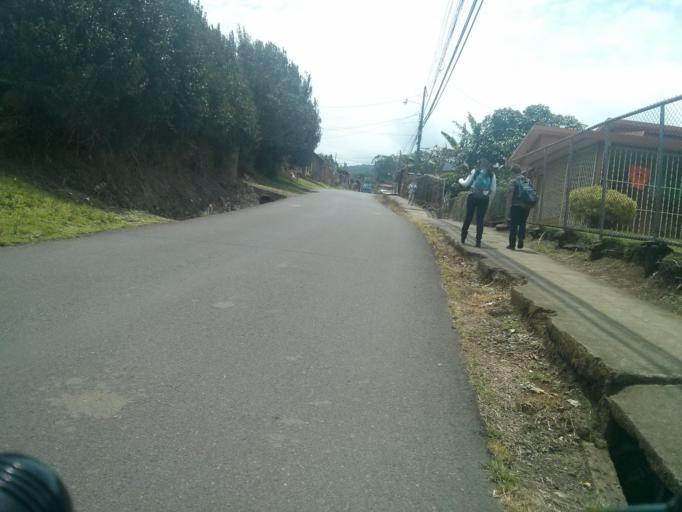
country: CR
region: Heredia
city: Angeles
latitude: 10.0209
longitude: -84.0383
